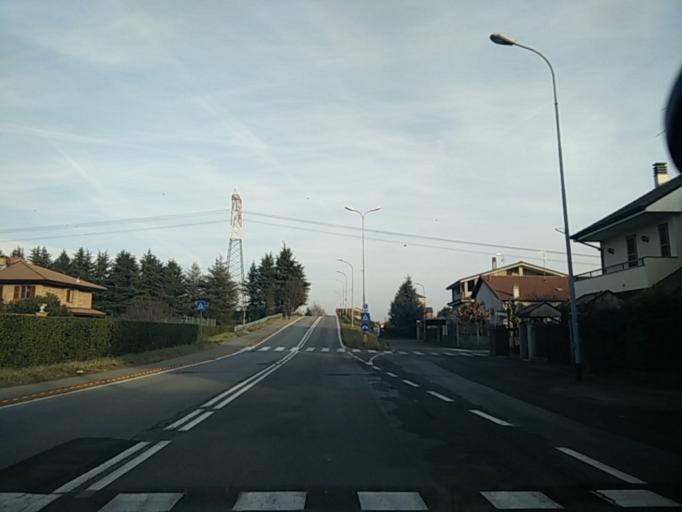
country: IT
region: Lombardy
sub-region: Provincia di Monza e Brianza
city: Cesano Maderno
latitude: 45.6244
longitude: 9.1627
